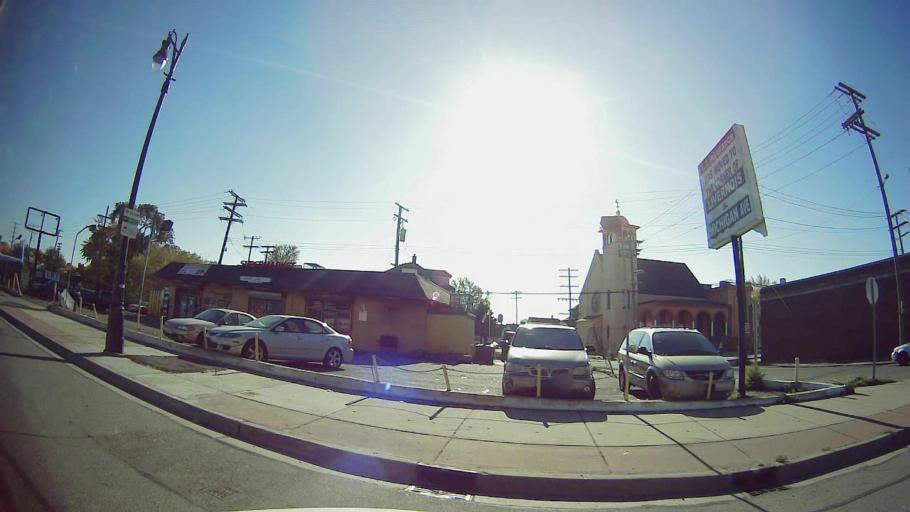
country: US
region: Michigan
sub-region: Wayne County
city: Dearborn
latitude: 42.3296
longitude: -83.1493
